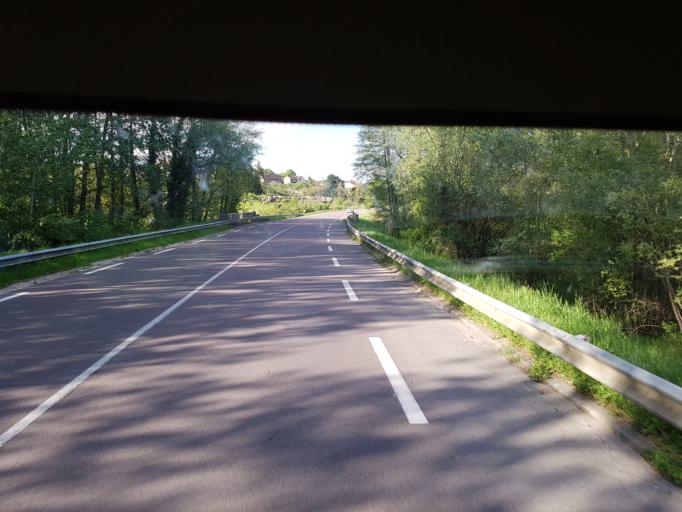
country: FR
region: Bourgogne
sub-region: Departement de l'Yonne
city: Saint-Florentin
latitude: 48.0008
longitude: 3.7356
